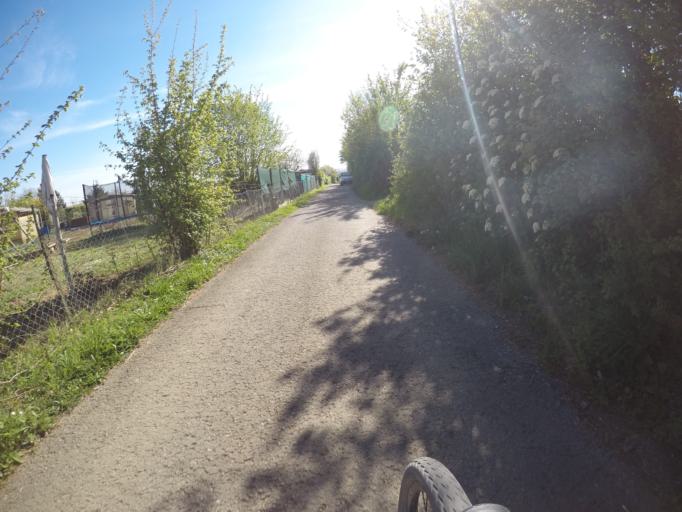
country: DE
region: Baden-Wuerttemberg
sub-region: Regierungsbezirk Stuttgart
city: Kornwestheim
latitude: 48.8539
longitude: 9.1942
